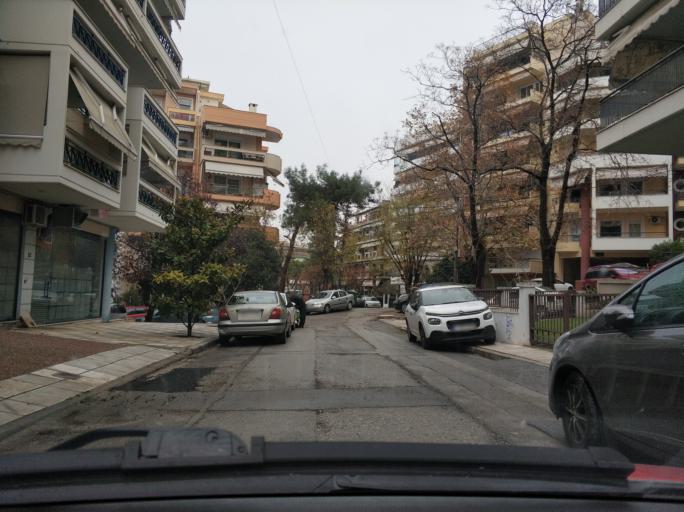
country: GR
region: Central Macedonia
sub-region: Nomos Thessalonikis
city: Pylaia
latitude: 40.5967
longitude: 22.9726
